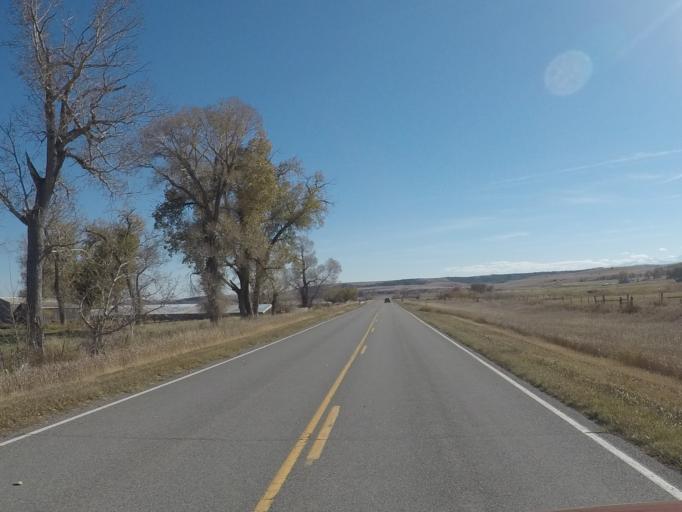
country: US
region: Montana
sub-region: Sweet Grass County
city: Big Timber
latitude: 45.8053
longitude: -109.8668
